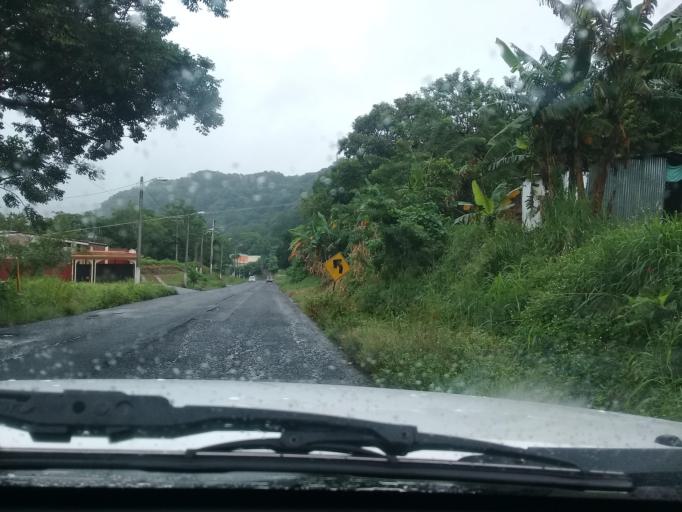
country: MX
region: Veracruz
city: Santiago Tuxtla
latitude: 18.4633
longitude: -95.2938
